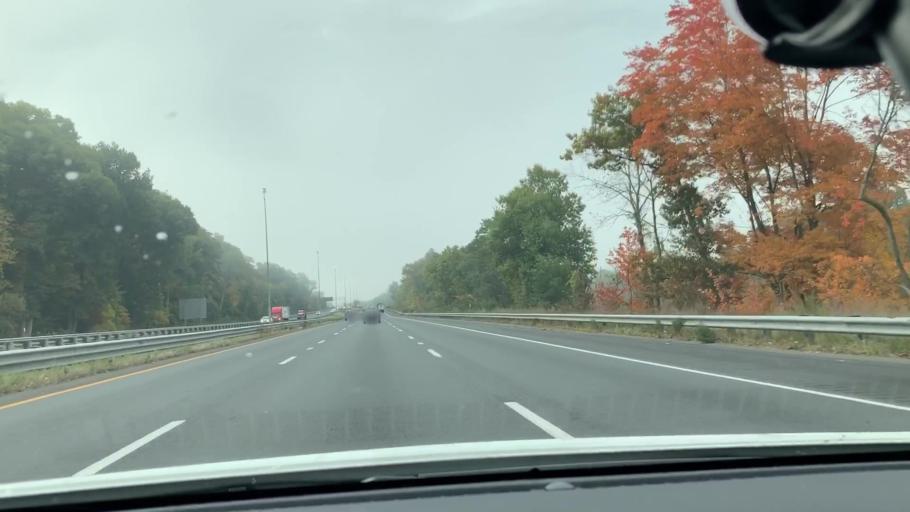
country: US
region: Massachusetts
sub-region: Hampden County
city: Longmeadow
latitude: 42.0637
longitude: -72.5890
